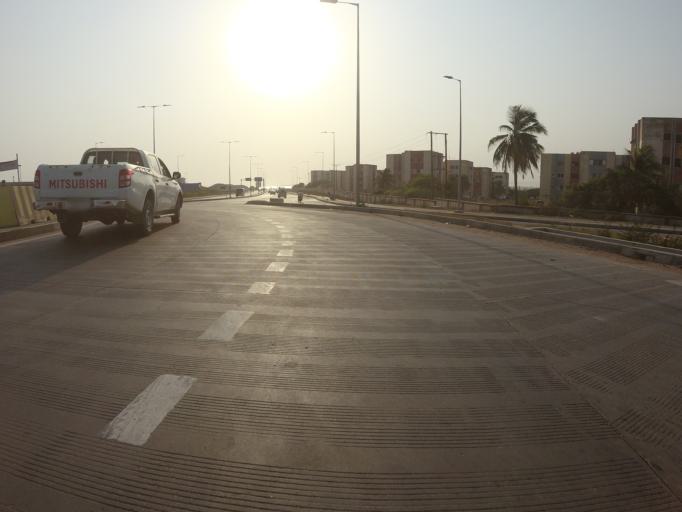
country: GH
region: Greater Accra
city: Tema
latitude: 5.6171
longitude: -0.0232
